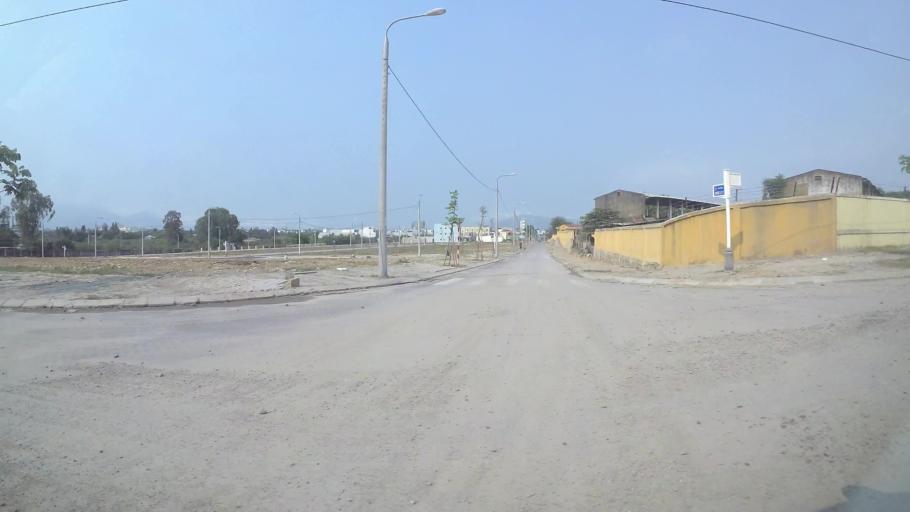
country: VN
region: Da Nang
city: Lien Chieu
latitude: 16.0423
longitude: 108.1633
